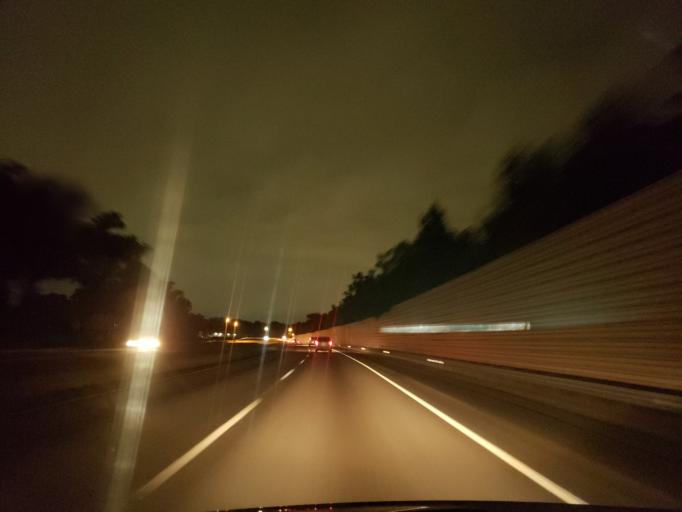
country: US
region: Georgia
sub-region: Chatham County
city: Thunderbolt
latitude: 32.0148
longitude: -81.0838
